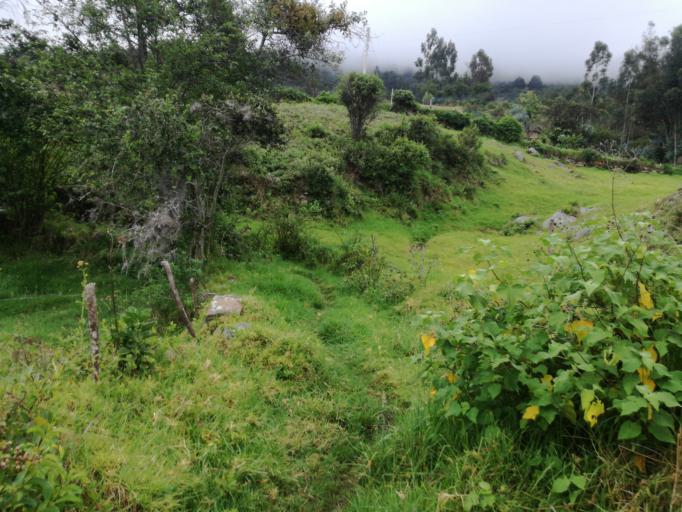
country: CO
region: Boyaca
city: Socha Viejo
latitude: 6.0039
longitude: -72.6832
